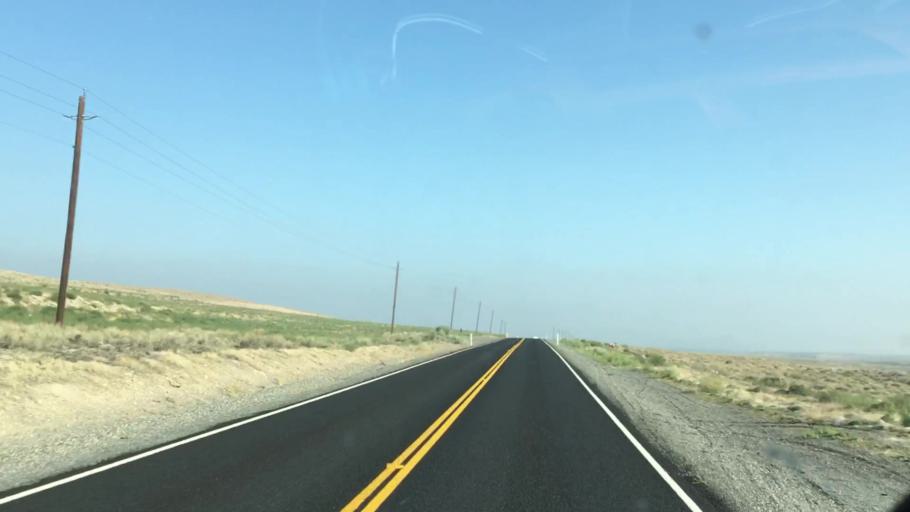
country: US
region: Nevada
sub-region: Lyon County
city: Fernley
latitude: 39.7646
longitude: -119.3412
